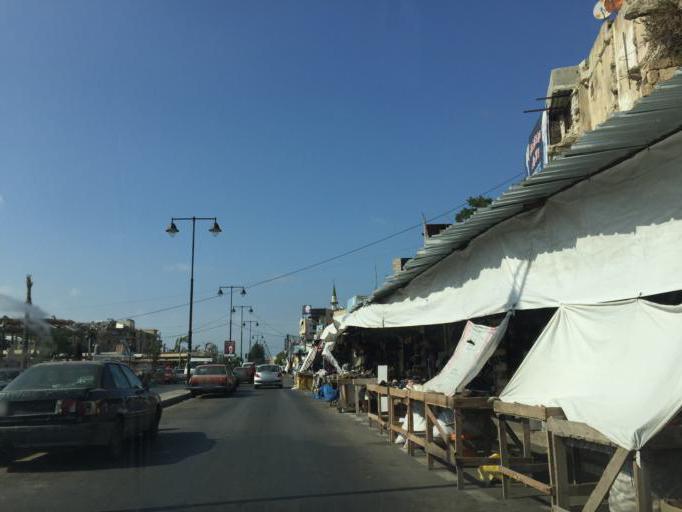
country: LB
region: Liban-Nord
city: Tripoli
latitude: 34.4372
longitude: 35.8471
